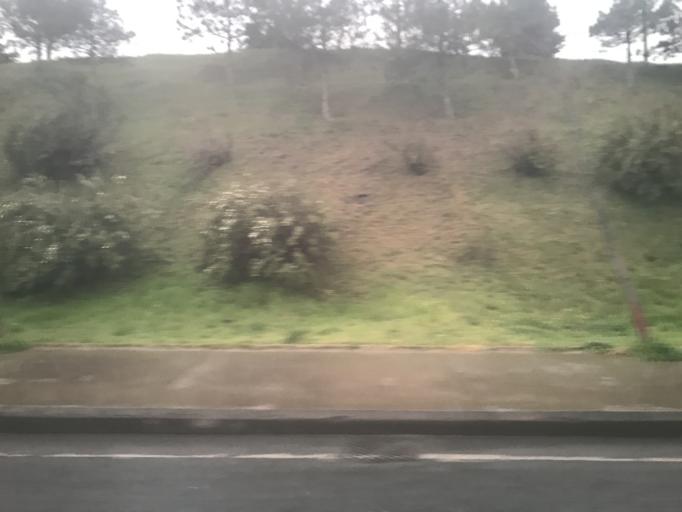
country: TR
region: Istanbul
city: Sisli
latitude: 41.0528
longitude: 28.9501
